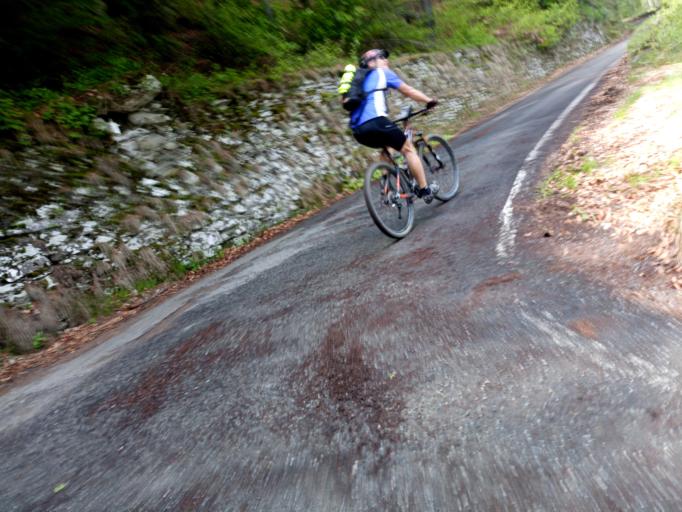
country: IT
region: Piedmont
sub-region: Provincia di Torino
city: Meana di Susa
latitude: 45.1080
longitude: 7.0747
